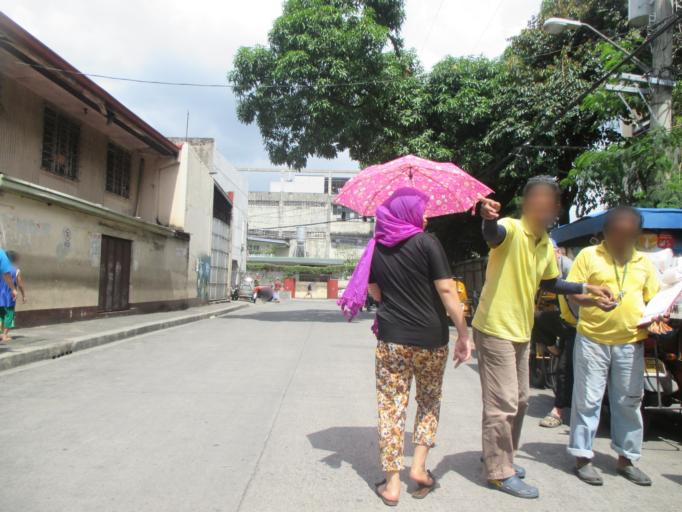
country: PH
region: Metro Manila
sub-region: Marikina
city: Calumpang
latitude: 14.6321
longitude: 121.0970
